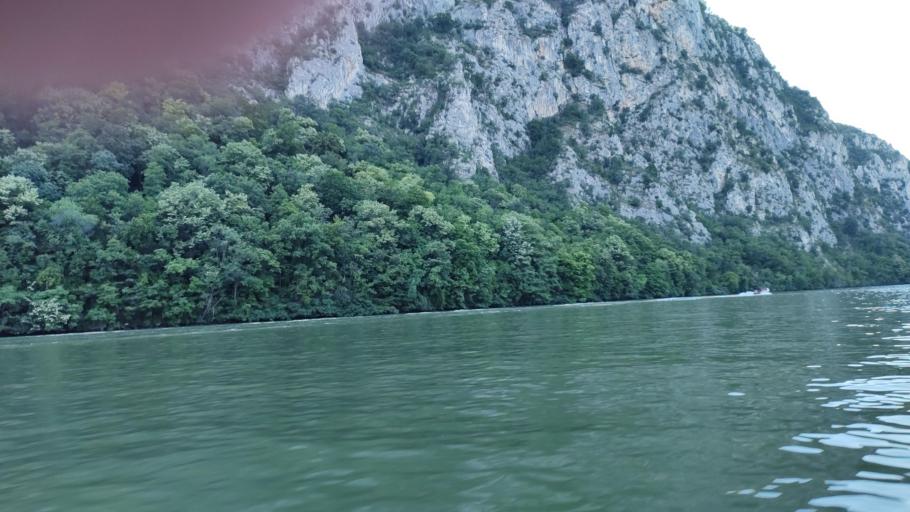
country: RO
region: Mehedinti
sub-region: Comuna Dubova
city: Dubova
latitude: 44.6048
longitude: 22.2678
